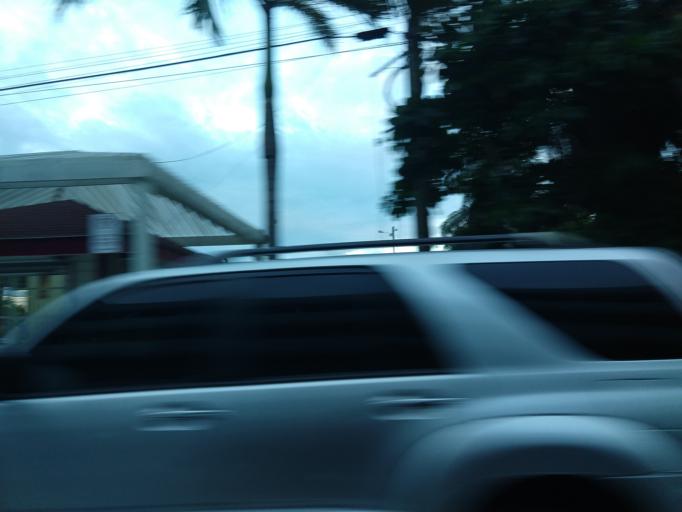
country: BZ
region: Belize
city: Belize City
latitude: 17.5066
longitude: -88.1883
